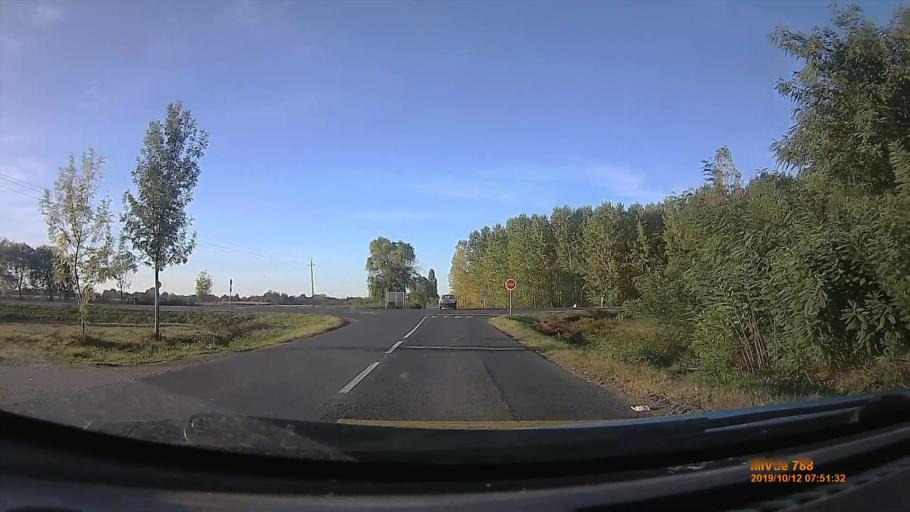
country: HU
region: Hajdu-Bihar
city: Biharkeresztes
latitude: 47.1402
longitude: 21.7302
